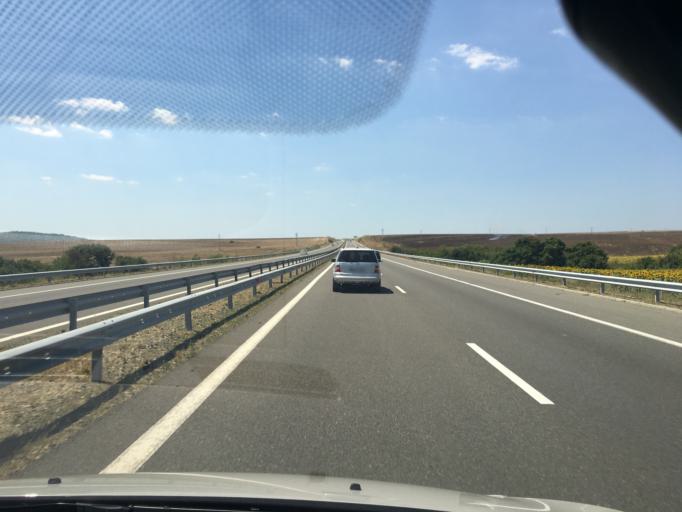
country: BG
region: Burgas
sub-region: Obshtina Karnobat
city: Karnobat
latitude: 42.5896
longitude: 26.9708
